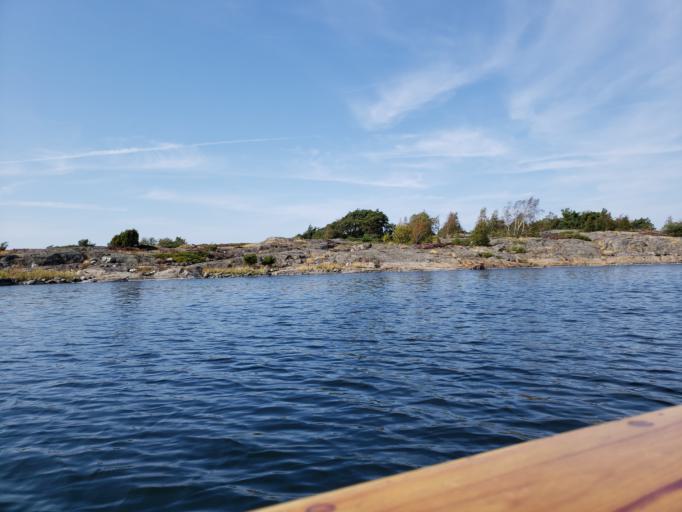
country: FI
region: Varsinais-Suomi
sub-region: Aboland-Turunmaa
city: Dragsfjaerd
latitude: 59.8479
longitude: 22.2078
